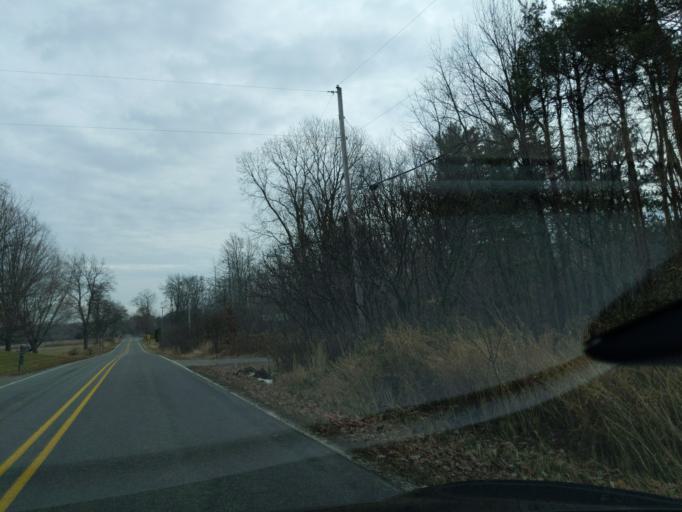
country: US
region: Michigan
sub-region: Ingham County
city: Leslie
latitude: 42.4649
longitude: -84.5207
